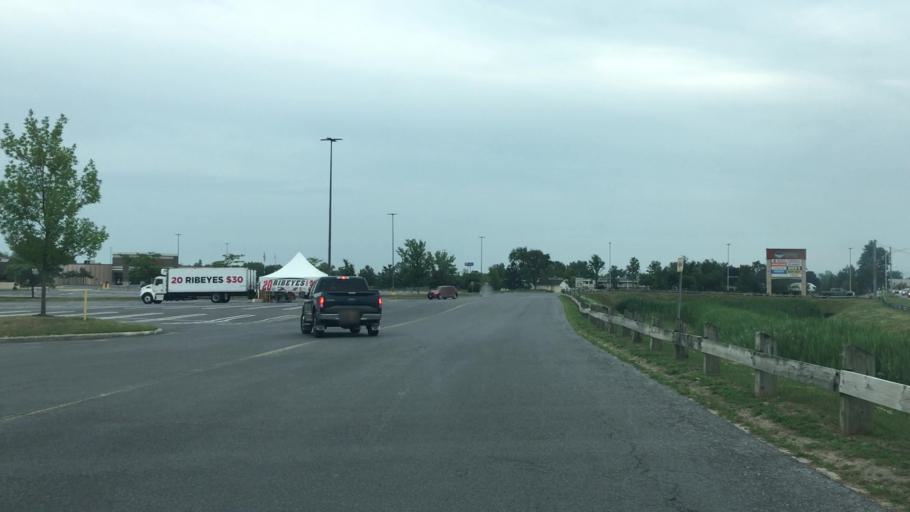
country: US
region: New York
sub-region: Clinton County
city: Plattsburgh West
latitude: 44.7021
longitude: -73.4937
